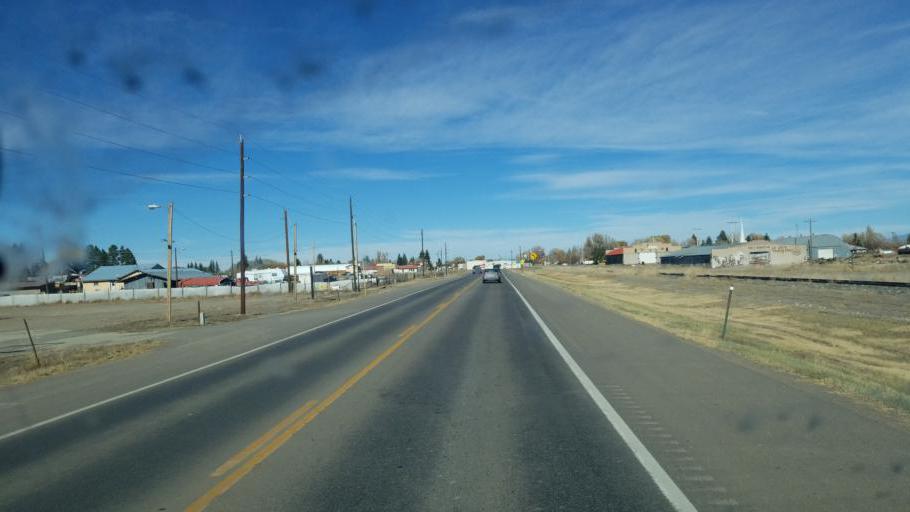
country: US
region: Colorado
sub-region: Conejos County
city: Conejos
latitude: 37.2659
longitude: -105.9636
